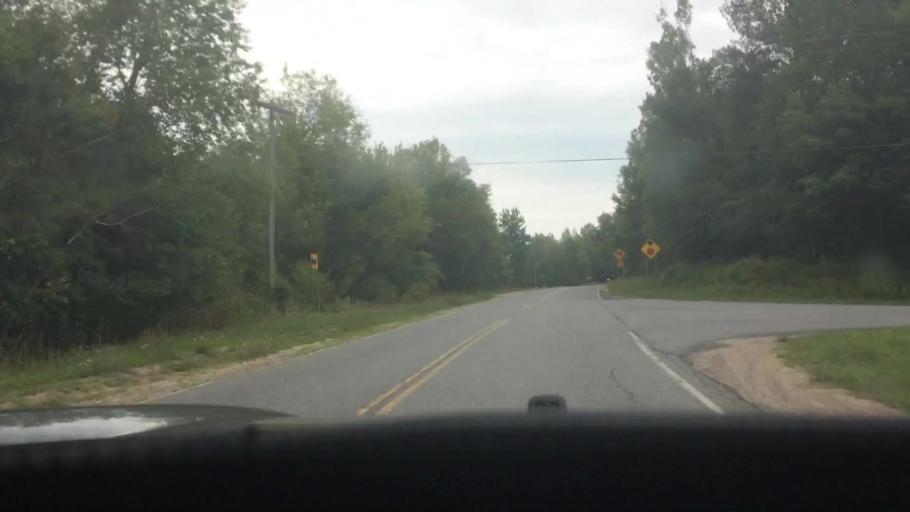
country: US
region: New York
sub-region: St. Lawrence County
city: Hannawa Falls
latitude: 44.6251
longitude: -74.8447
